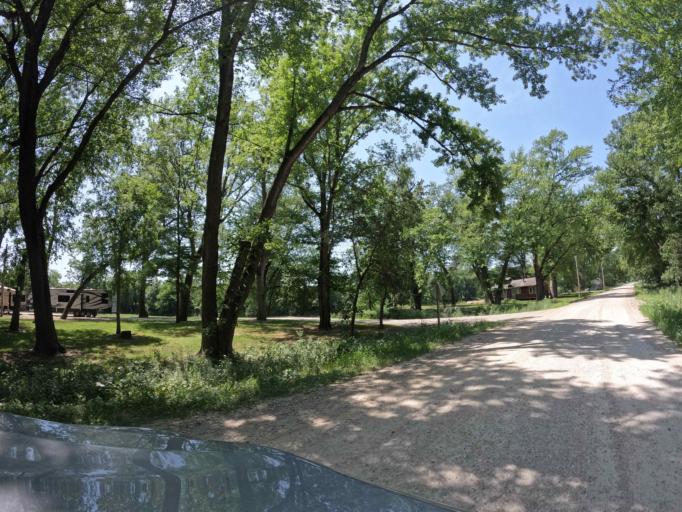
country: US
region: Iowa
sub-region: Henry County
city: Mount Pleasant
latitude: 40.9326
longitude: -91.6006
